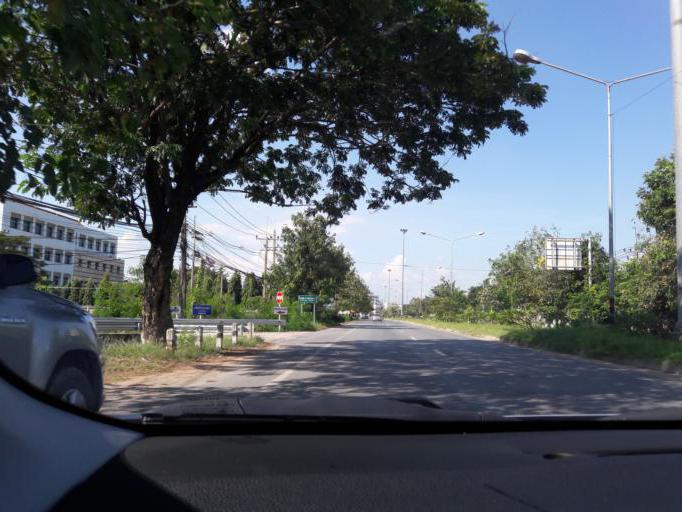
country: TH
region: Ang Thong
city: Ang Thong
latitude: 14.5778
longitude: 100.4533
